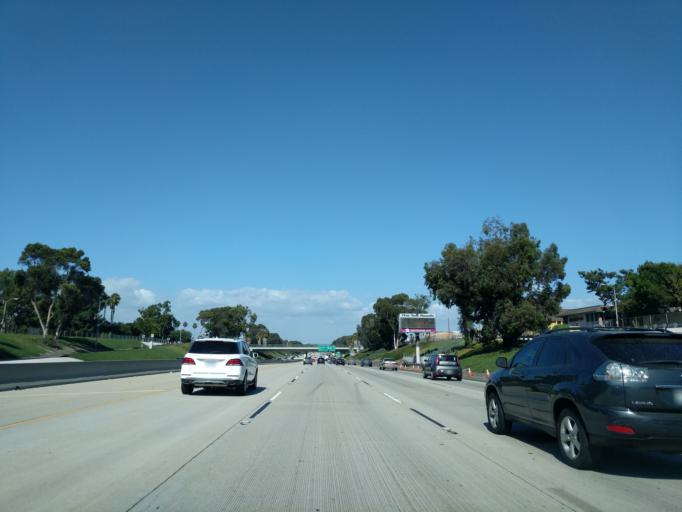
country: US
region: California
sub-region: Orange County
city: Costa Mesa
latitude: 33.6608
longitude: -117.8998
